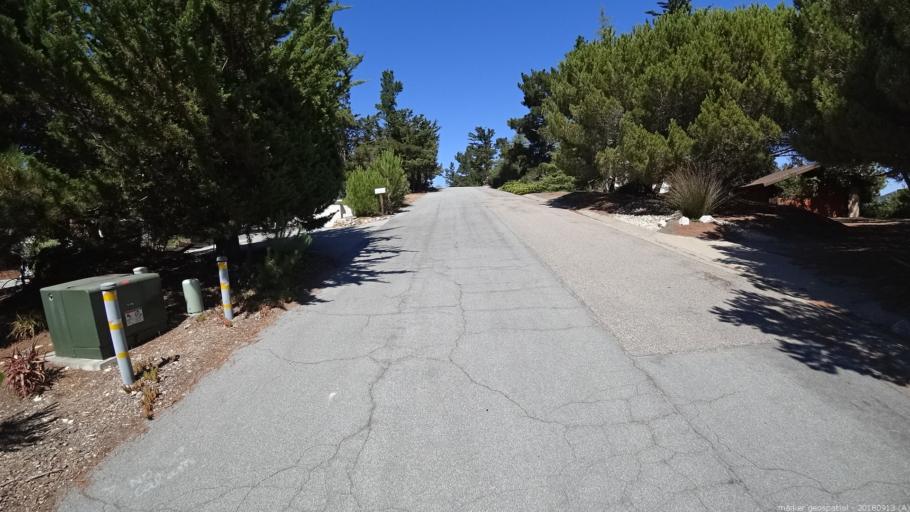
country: US
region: California
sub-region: Monterey County
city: Carmel Valley Village
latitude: 36.5399
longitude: -121.7967
